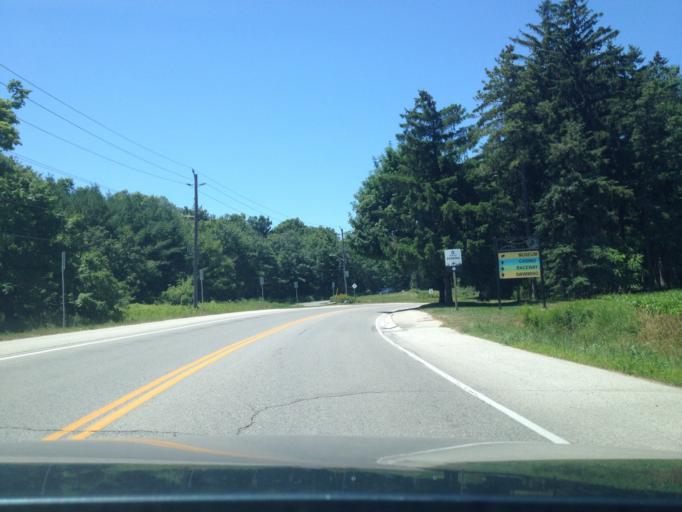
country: CA
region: Ontario
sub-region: Wellington County
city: Guelph
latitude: 43.6907
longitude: -80.3938
